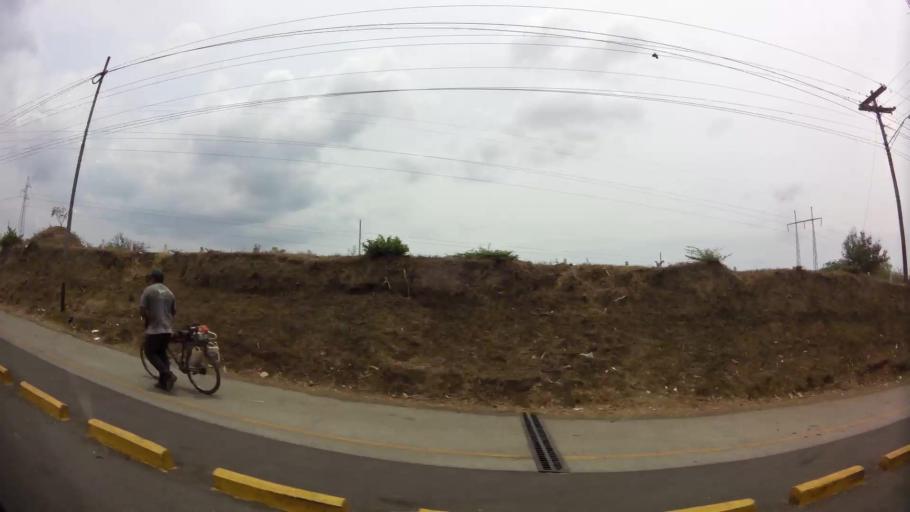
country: NI
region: Leon
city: Leon
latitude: 12.4397
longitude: -86.8632
